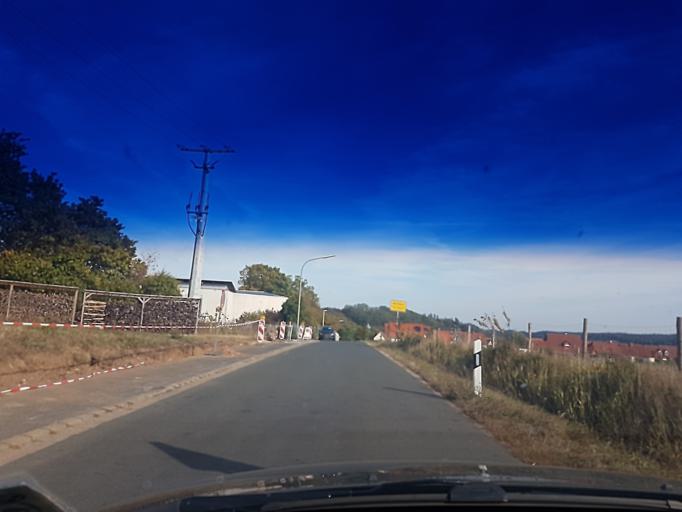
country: DE
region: Bavaria
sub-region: Regierungsbezirk Mittelfranken
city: Burghaslach
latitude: 49.7744
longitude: 10.5557
